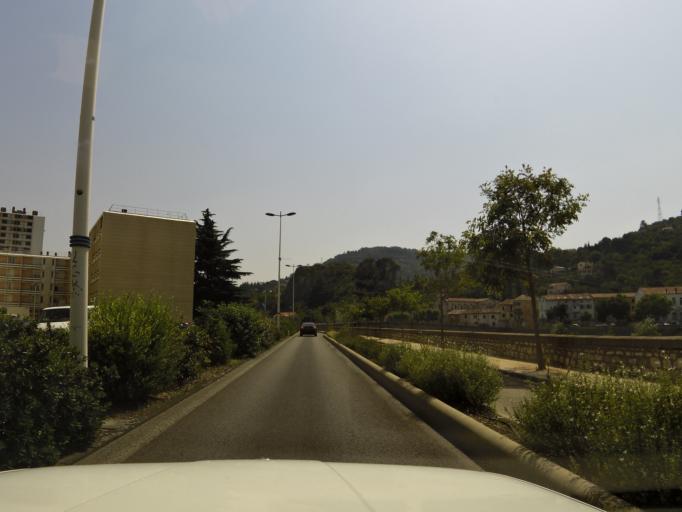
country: FR
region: Languedoc-Roussillon
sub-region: Departement du Gard
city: Ales
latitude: 44.1255
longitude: 4.0729
